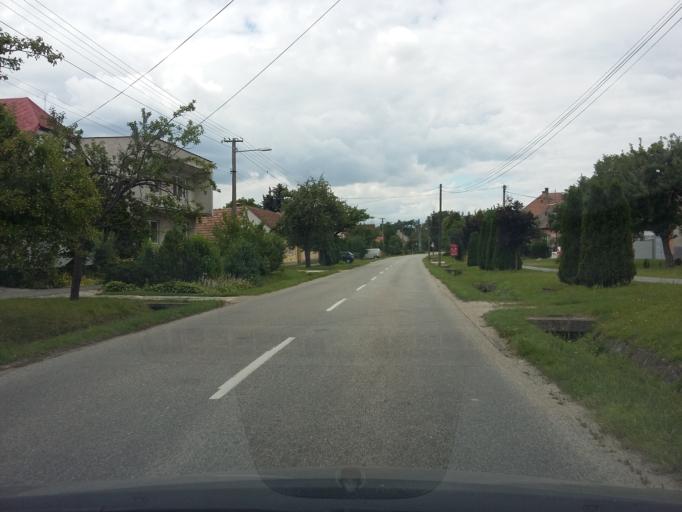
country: SK
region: Trnavsky
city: Smolenice
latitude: 48.5588
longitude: 17.3469
